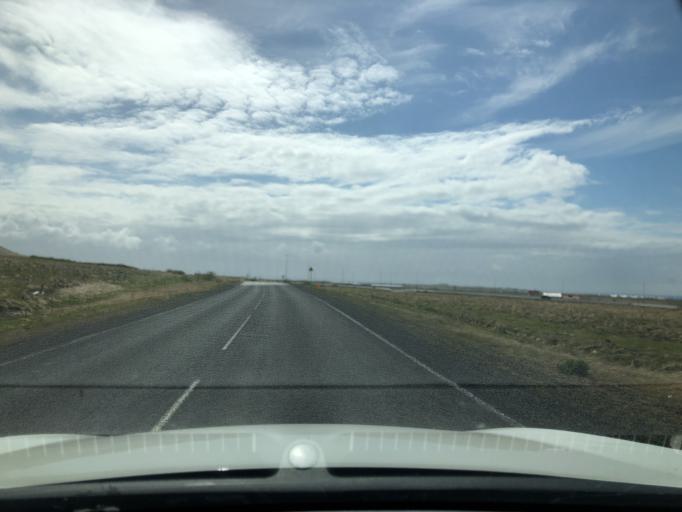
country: IS
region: Capital Region
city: Reykjavik
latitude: 64.2775
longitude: -21.8354
